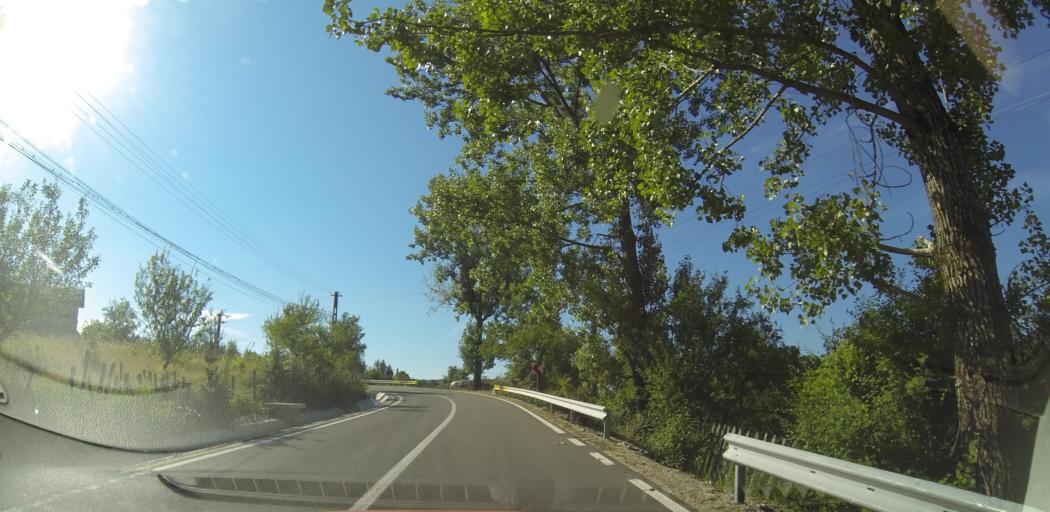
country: RO
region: Valcea
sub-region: Comuna Vaideeni
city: Vaideeni
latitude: 45.1686
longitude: 23.8801
